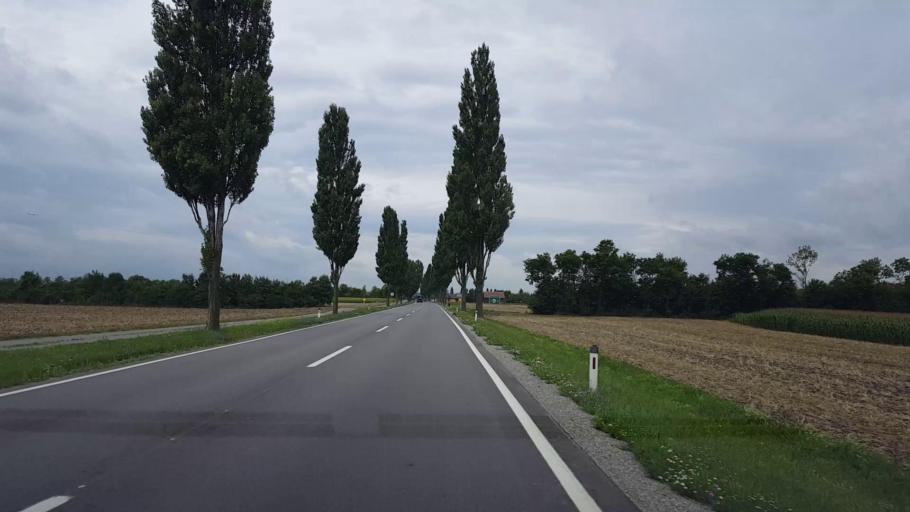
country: AT
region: Lower Austria
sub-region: Politischer Bezirk Bruck an der Leitha
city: Trautmannsdorf an der Leitha
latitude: 48.0492
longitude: 16.6497
